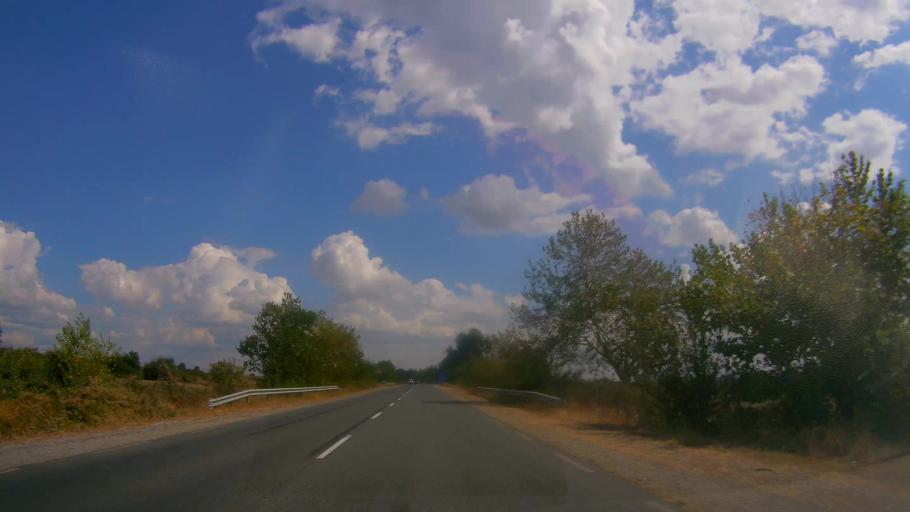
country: BG
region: Sliven
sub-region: Obshtina Sliven
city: Kermen
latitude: 42.6324
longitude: 26.1711
